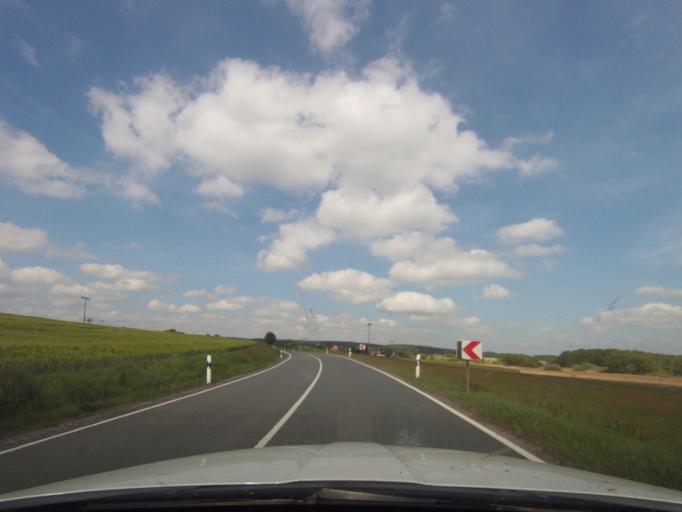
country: DE
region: Thuringia
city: Renthendorf
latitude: 50.7807
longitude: 11.9470
